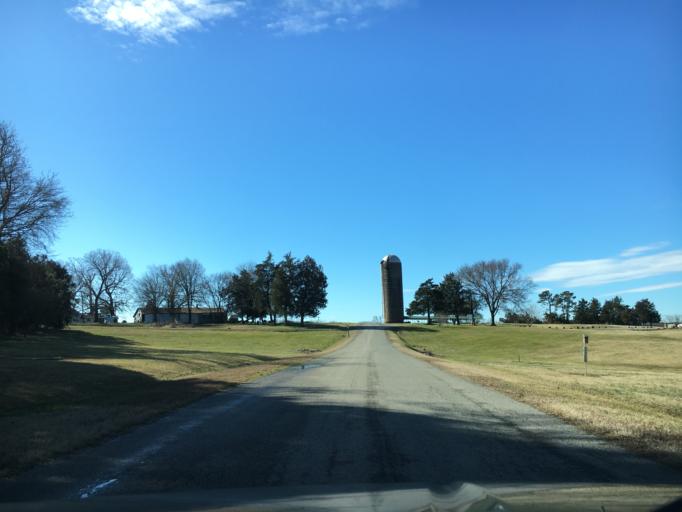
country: US
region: Virginia
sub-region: Halifax County
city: South Boston
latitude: 36.7189
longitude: -78.8662
